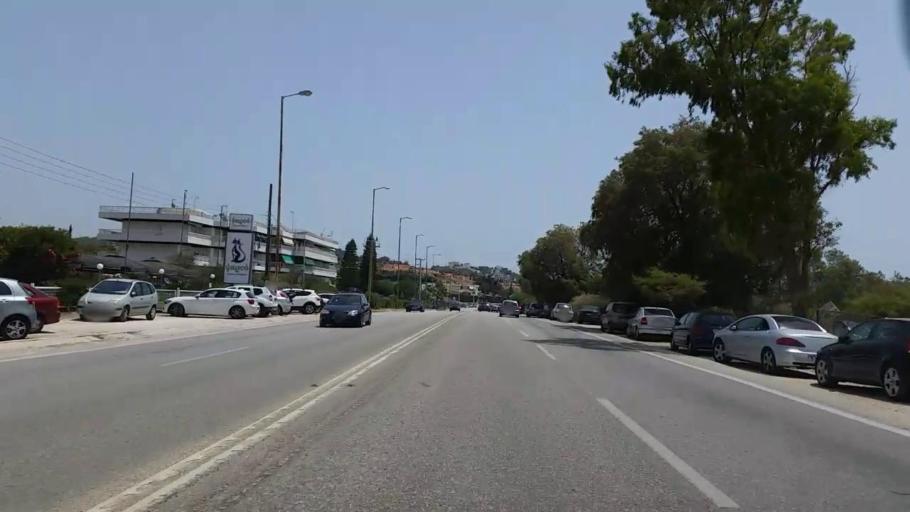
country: GR
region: Attica
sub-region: Nomarchia Anatolikis Attikis
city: Saronida
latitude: 37.7391
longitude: 23.9048
